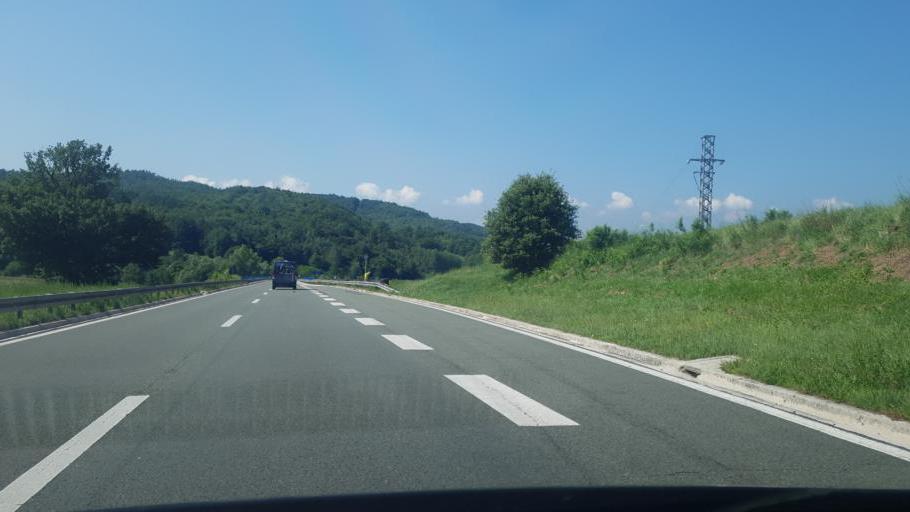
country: HR
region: Istarska
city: Buzet
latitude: 45.3083
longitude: 14.0631
